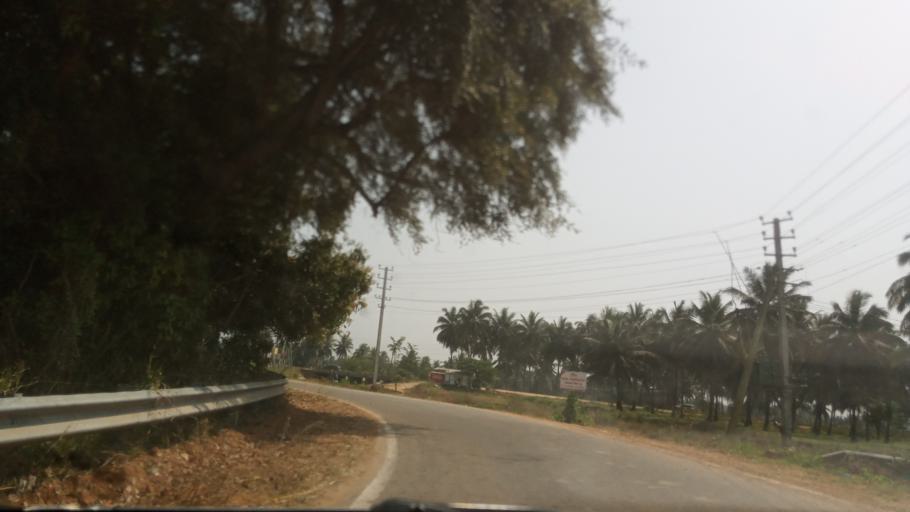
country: IN
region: Karnataka
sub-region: Mandya
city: Shrirangapattana
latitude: 12.4180
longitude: 76.6605
